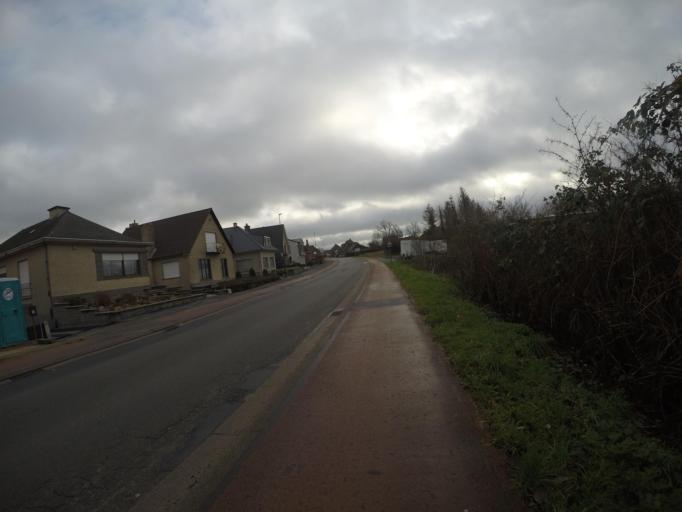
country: BE
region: Flanders
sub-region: Provincie Vlaams-Brabant
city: Ledeberg
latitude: 50.8374
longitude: 4.0834
